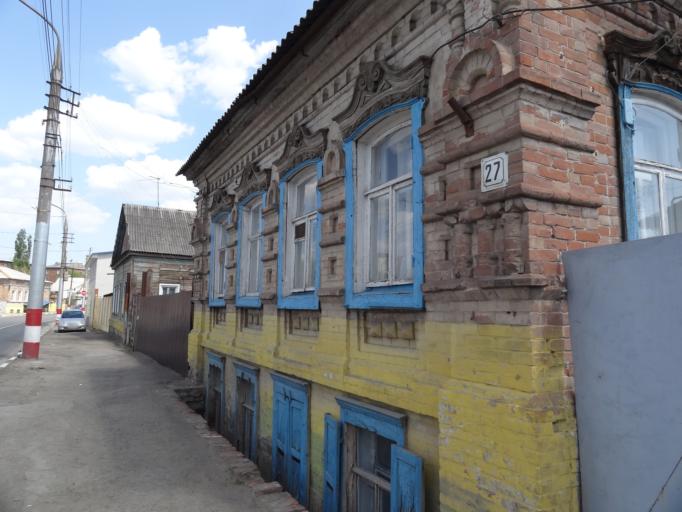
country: RU
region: Saratov
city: Engel's
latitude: 51.5033
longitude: 46.1128
